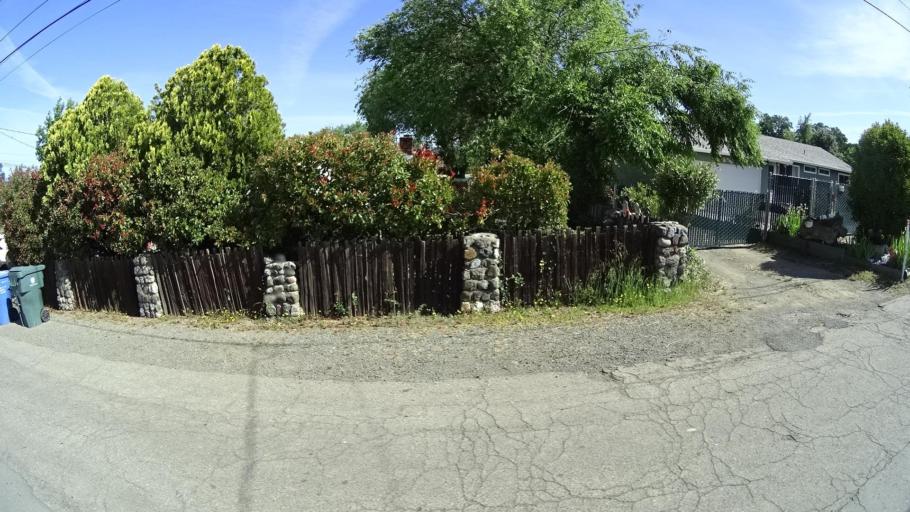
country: US
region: California
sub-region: Lake County
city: Kelseyville
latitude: 38.9675
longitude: -122.8307
